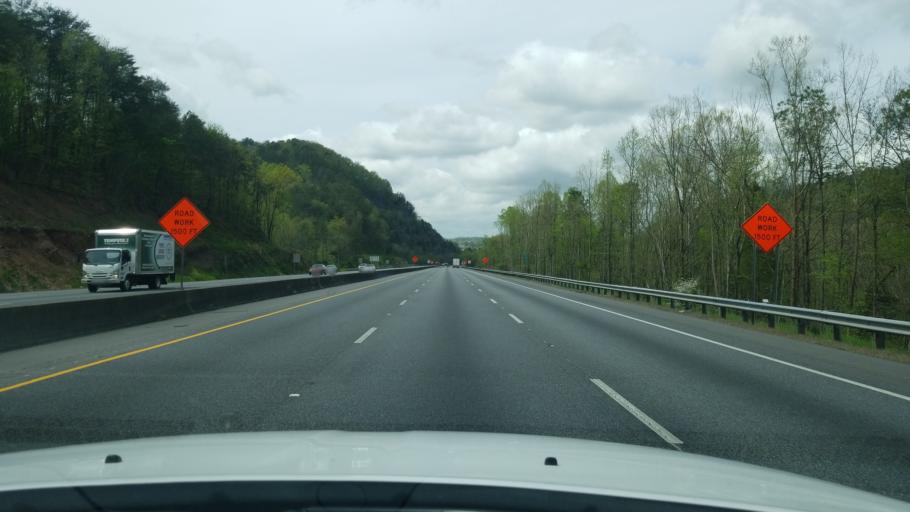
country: US
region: Georgia
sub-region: Catoosa County
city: Ringgold
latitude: 34.9047
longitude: -85.0938
